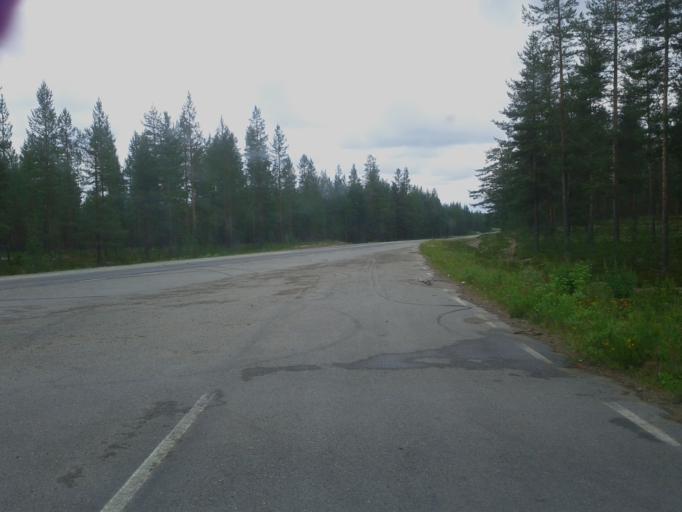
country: SE
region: Vaesterbotten
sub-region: Skelleftea Kommun
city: Storvik
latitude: 65.1104
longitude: 20.7739
